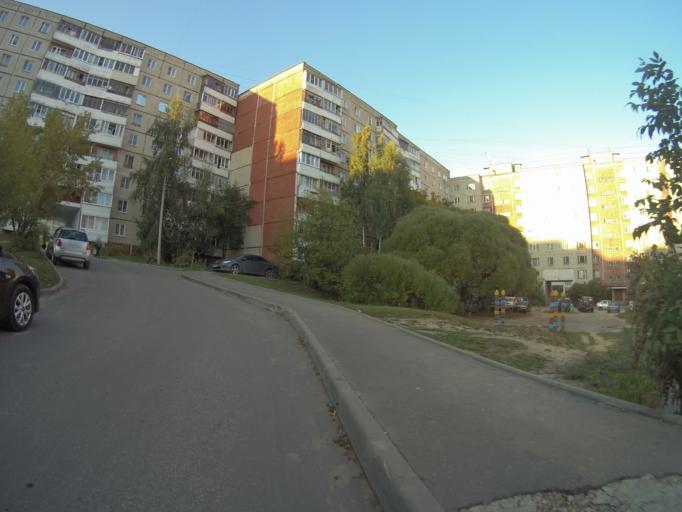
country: RU
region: Vladimir
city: Vladimir
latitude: 56.1092
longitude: 40.3530
